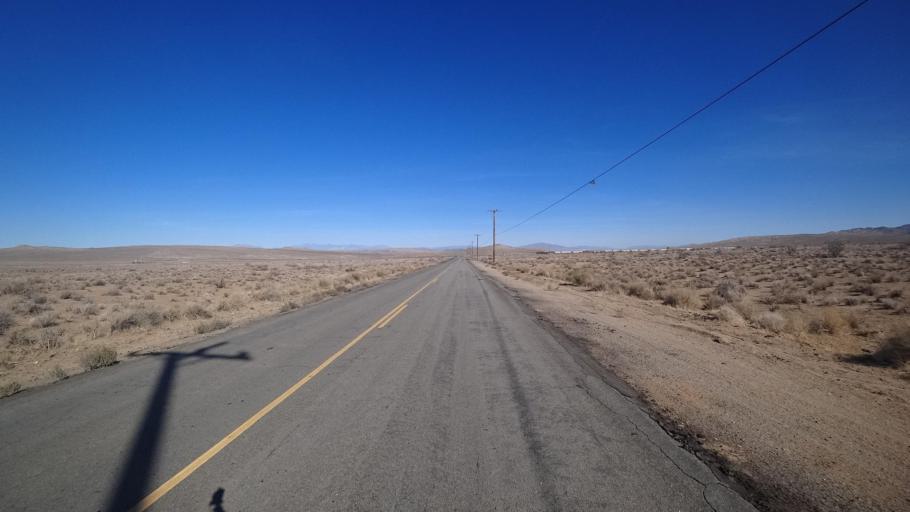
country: US
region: California
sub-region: Kern County
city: Ridgecrest
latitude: 35.4825
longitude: -117.6432
